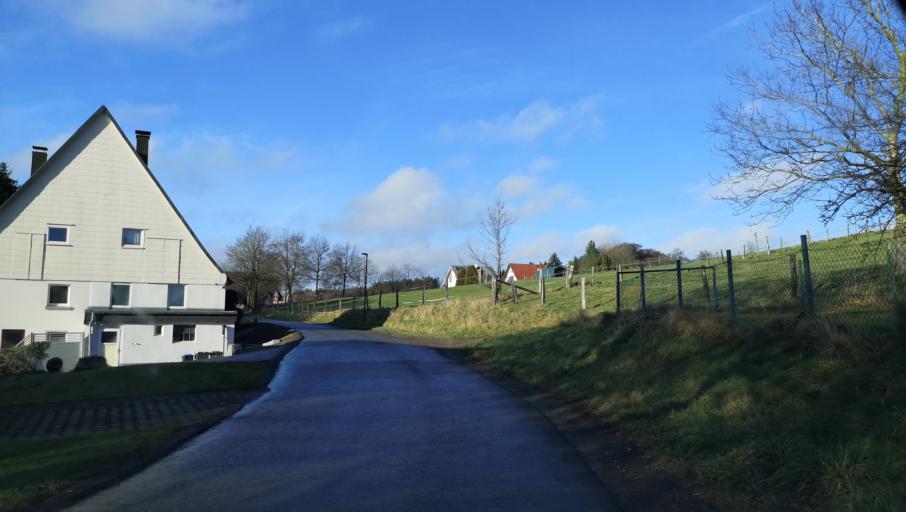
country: DE
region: North Rhine-Westphalia
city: Halver
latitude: 51.1852
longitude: 7.4353
